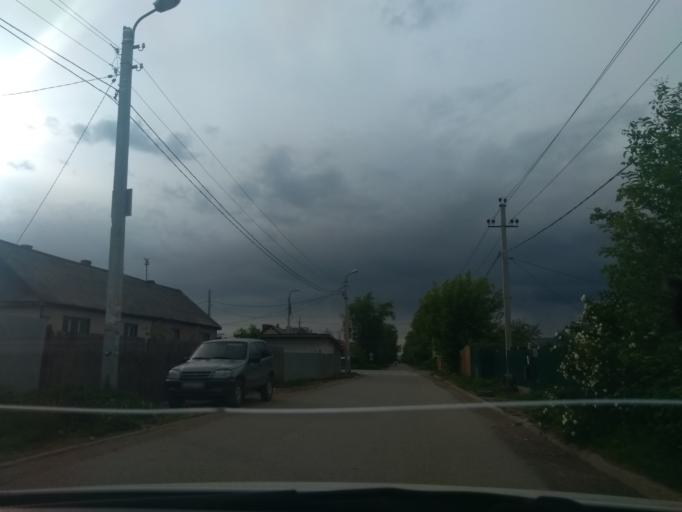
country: RU
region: Perm
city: Perm
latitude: 57.9964
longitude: 56.3369
